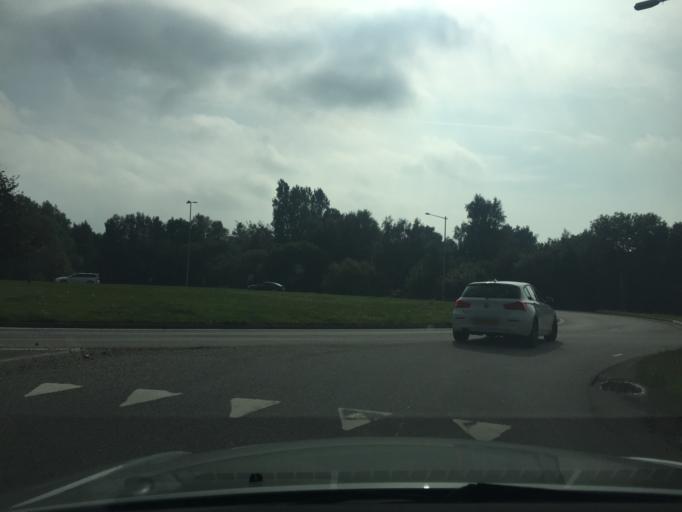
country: SE
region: Skane
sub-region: Kavlinge Kommun
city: Hofterup
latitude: 55.7658
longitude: 12.9847
